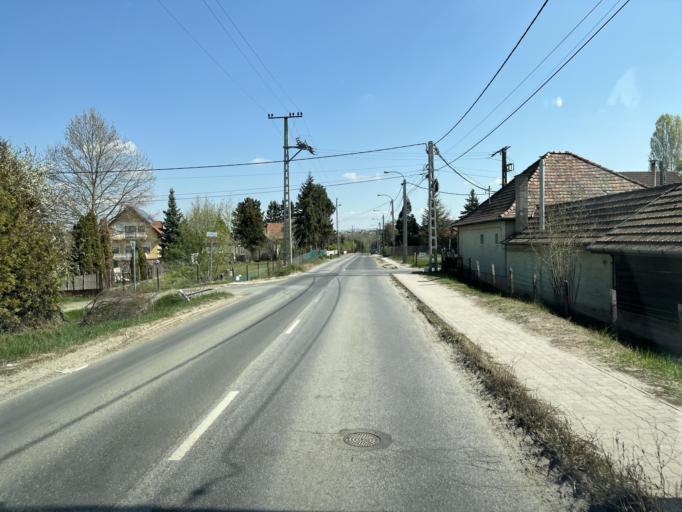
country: HU
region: Pest
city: Orbottyan
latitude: 47.6883
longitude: 19.2843
